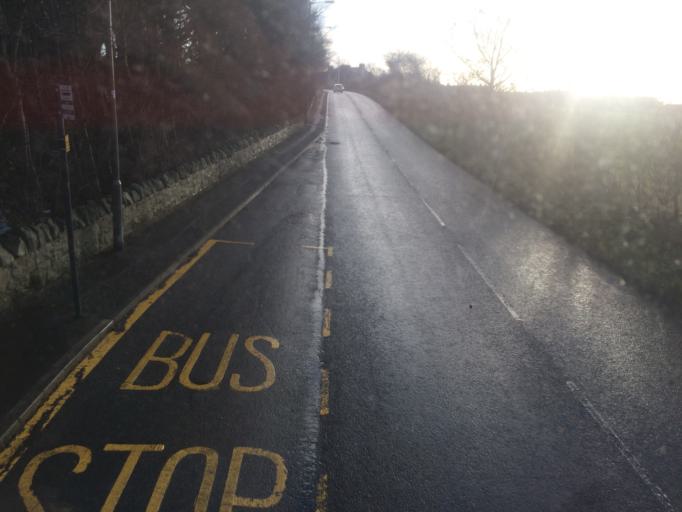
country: GB
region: Scotland
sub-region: Midlothian
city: Loanhead
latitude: 55.8616
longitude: -3.1693
